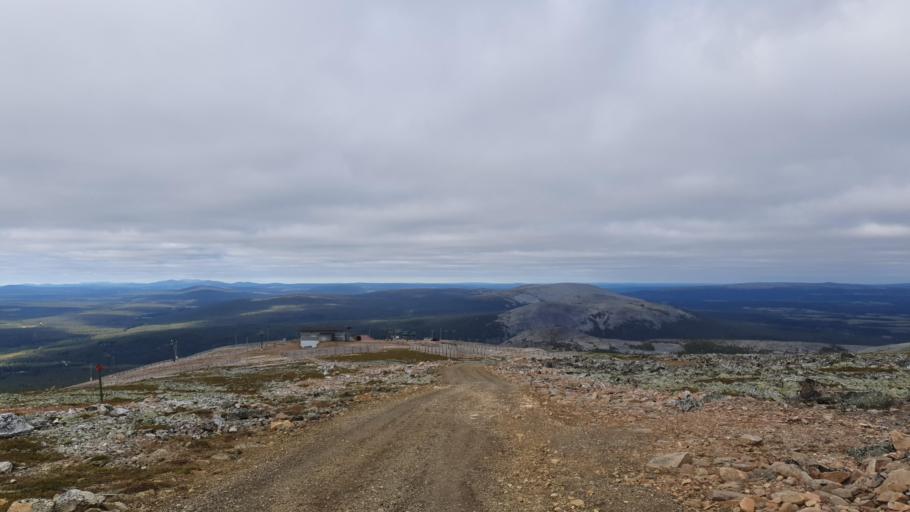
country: FI
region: Lapland
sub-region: Tunturi-Lappi
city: Kolari
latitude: 67.5677
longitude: 24.2095
